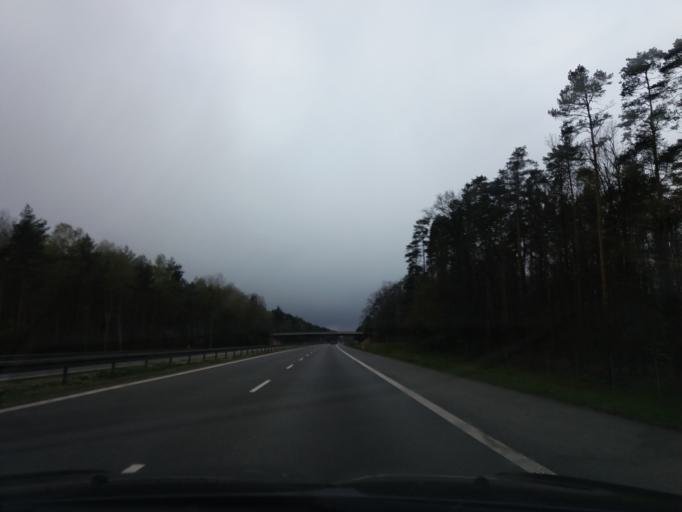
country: PL
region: Opole Voivodeship
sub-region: Powiat opolski
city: Proszkow
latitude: 50.5826
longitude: 17.8285
